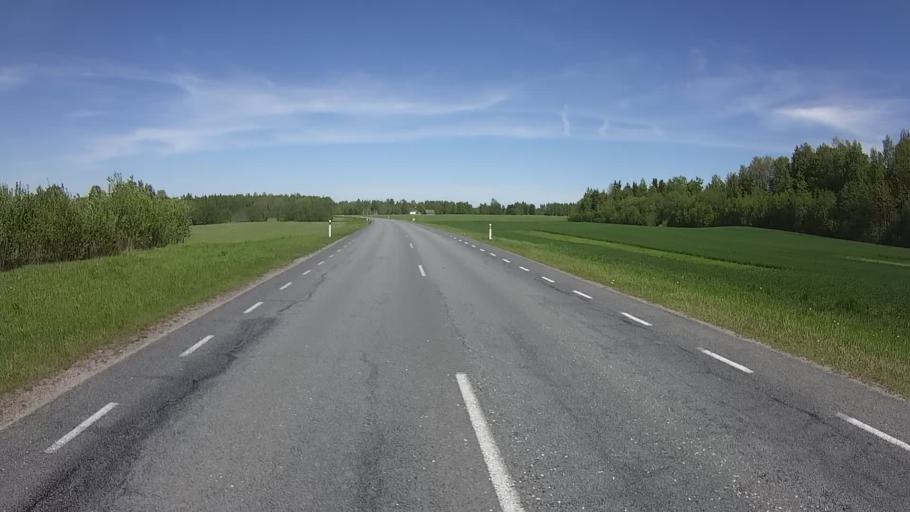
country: LV
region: Apes Novads
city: Ape
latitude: 57.6719
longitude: 26.7232
